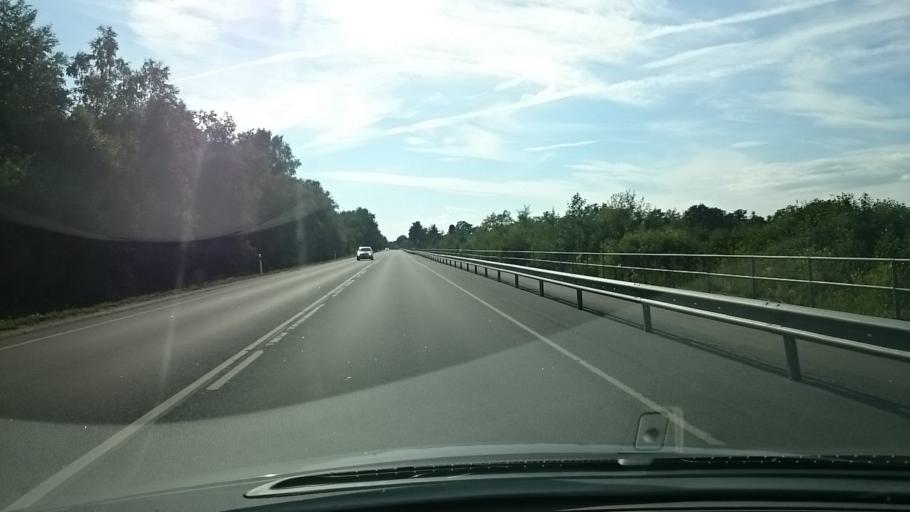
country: EE
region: Laeaene
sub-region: Ridala Parish
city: Uuemoisa
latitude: 58.9490
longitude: 23.6361
